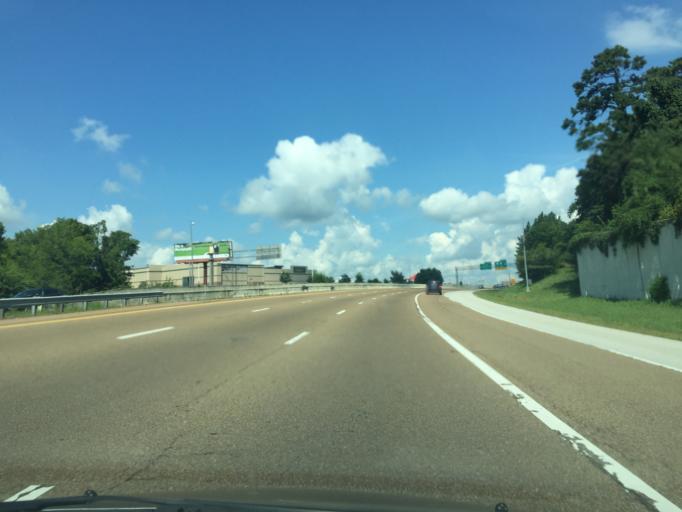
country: US
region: Tennessee
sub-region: Hamilton County
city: East Brainerd
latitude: 35.0292
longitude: -85.1782
